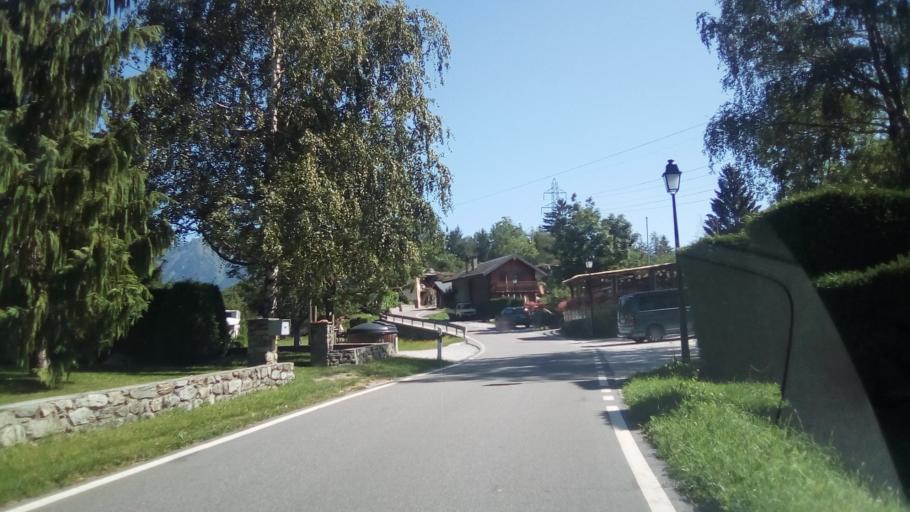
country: CH
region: Valais
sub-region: Saint-Maurice District
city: Salvan
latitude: 46.1078
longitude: 7.0068
